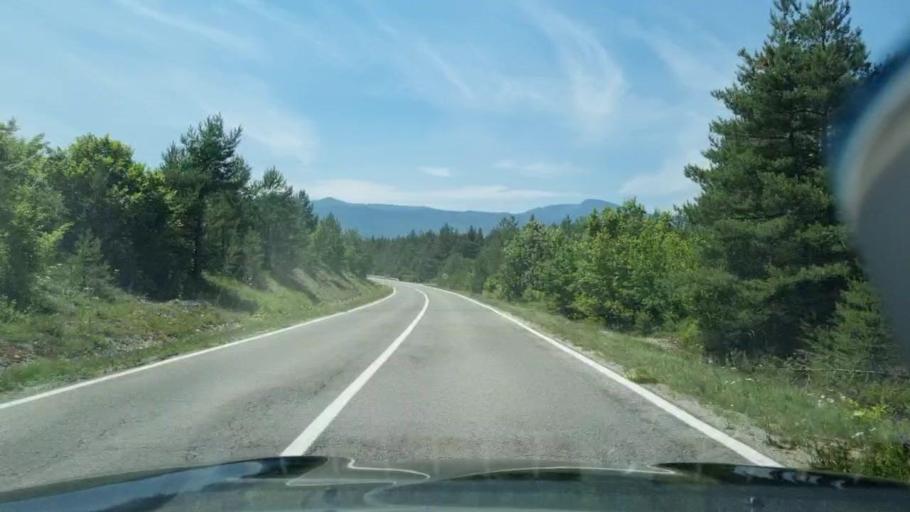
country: BA
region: Federation of Bosnia and Herzegovina
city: Sanica
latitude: 44.5422
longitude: 16.4091
